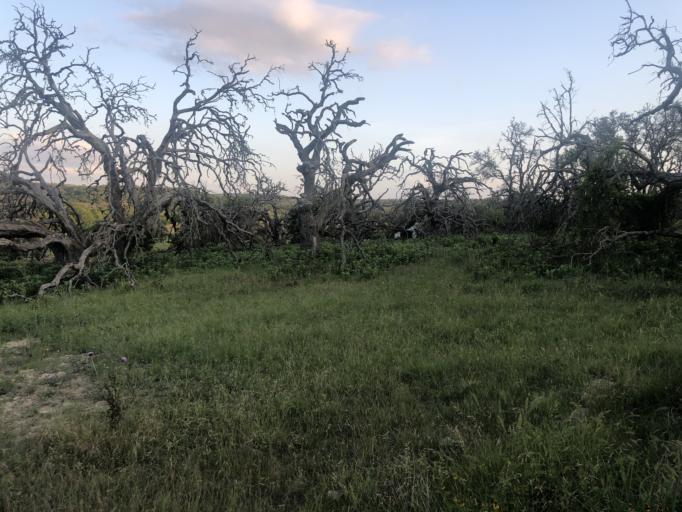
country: US
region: Texas
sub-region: Gillespie County
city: Fredericksburg
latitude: 30.1305
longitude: -98.7307
